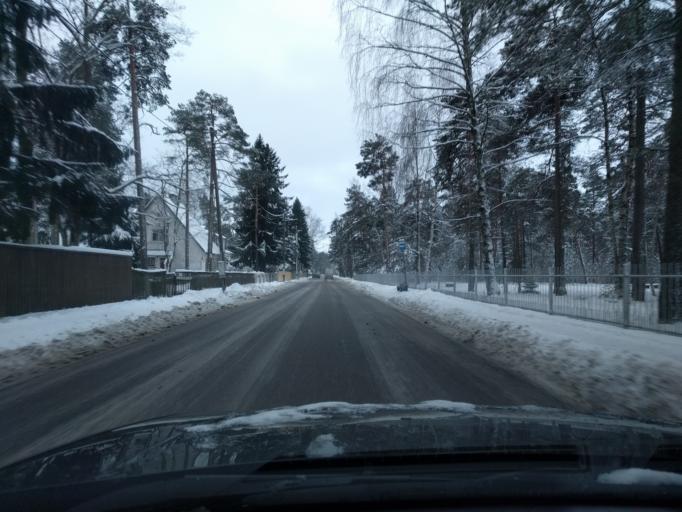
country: EE
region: Harju
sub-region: Saue vald
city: Laagri
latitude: 59.3803
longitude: 24.6682
